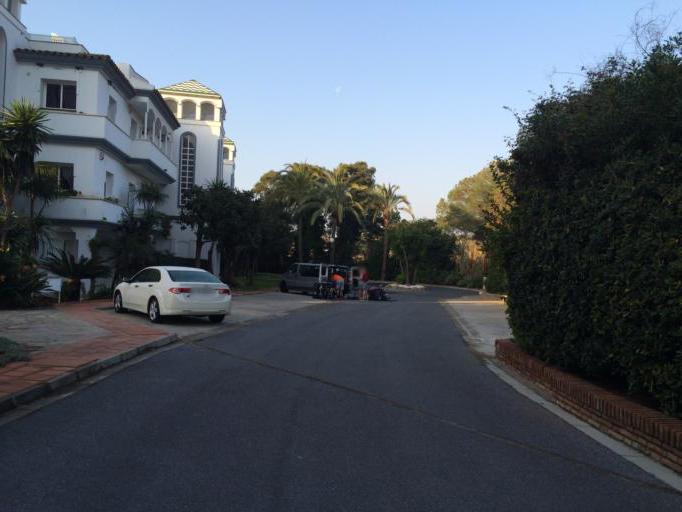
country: ES
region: Andalusia
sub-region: Provincia de Malaga
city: Estepona
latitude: 36.4440
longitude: -5.0940
